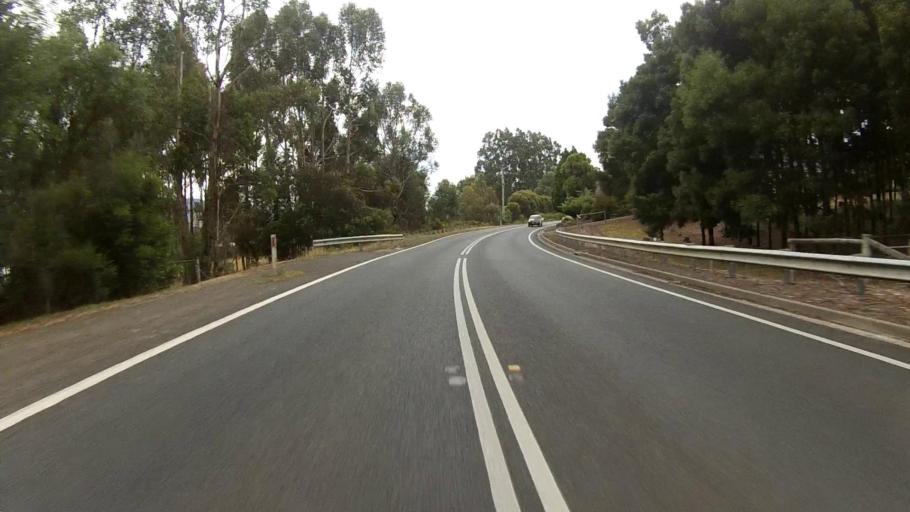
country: AU
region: Tasmania
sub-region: Huon Valley
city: Franklin
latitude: -43.0770
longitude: 147.0331
